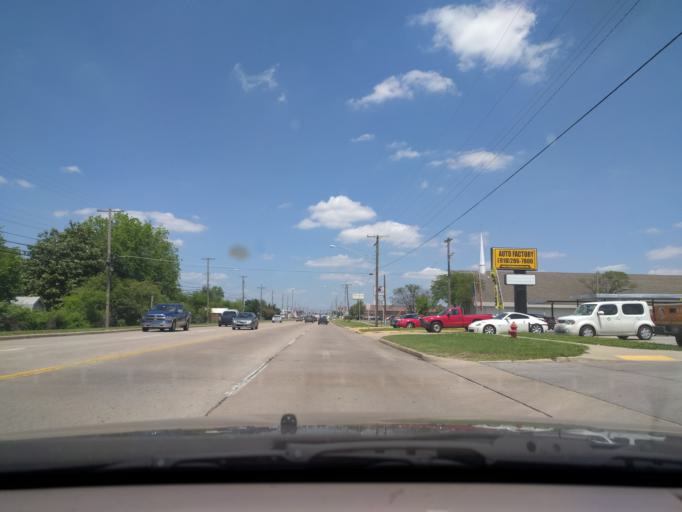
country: US
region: Oklahoma
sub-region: Tulsa County
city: Broken Arrow
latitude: 36.0640
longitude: -95.7974
